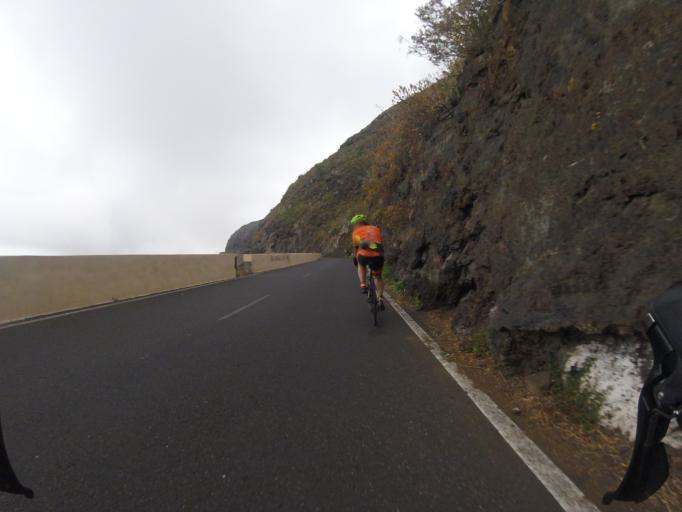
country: ES
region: Canary Islands
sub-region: Provincia de Santa Cruz de Tenerife
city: Guimar
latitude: 28.2936
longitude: -16.4076
